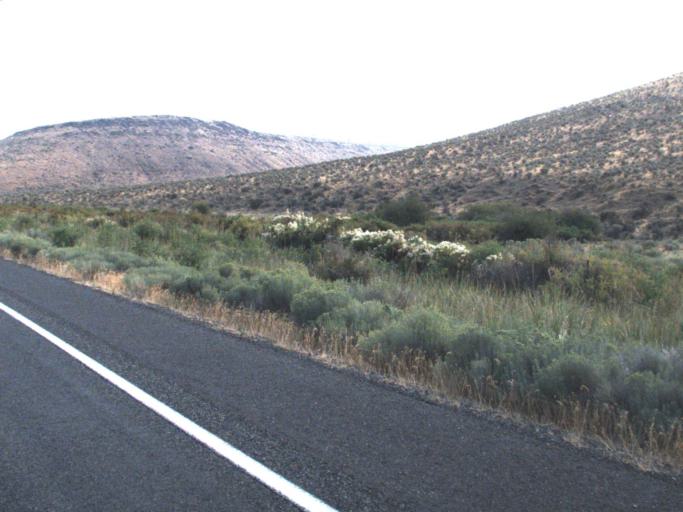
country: US
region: Washington
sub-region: Yakima County
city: Toppenish
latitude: 46.2227
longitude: -120.4300
